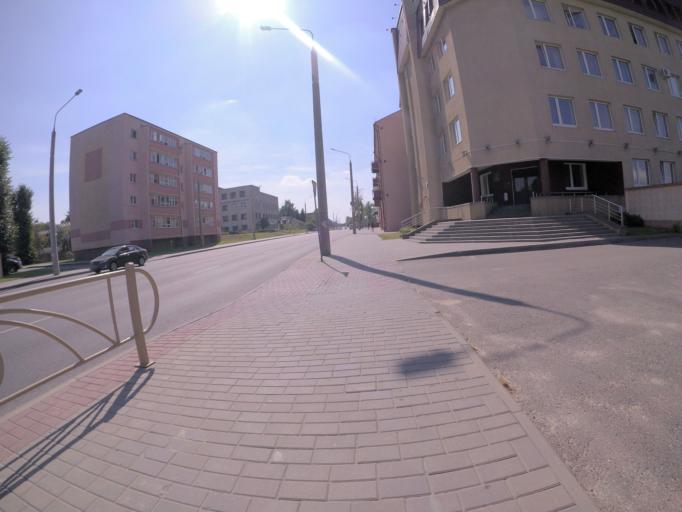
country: BY
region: Grodnenskaya
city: Hrodna
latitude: 53.6823
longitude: 23.8443
